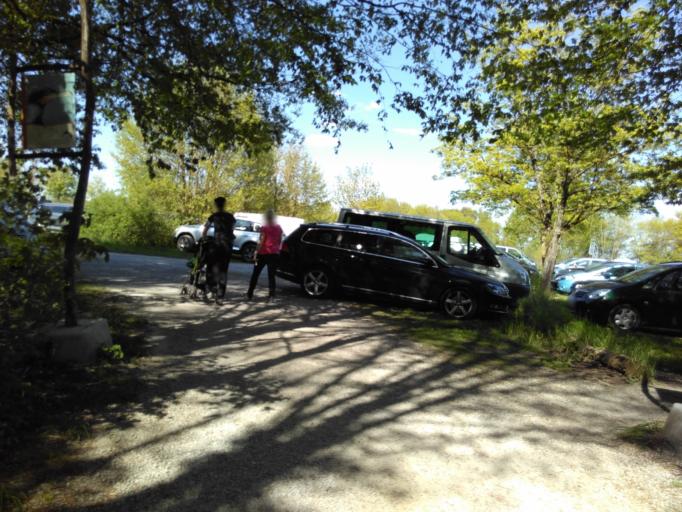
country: DE
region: Baden-Wuerttemberg
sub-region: Regierungsbezirk Stuttgart
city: Igersheim
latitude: 49.4691
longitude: 9.7983
